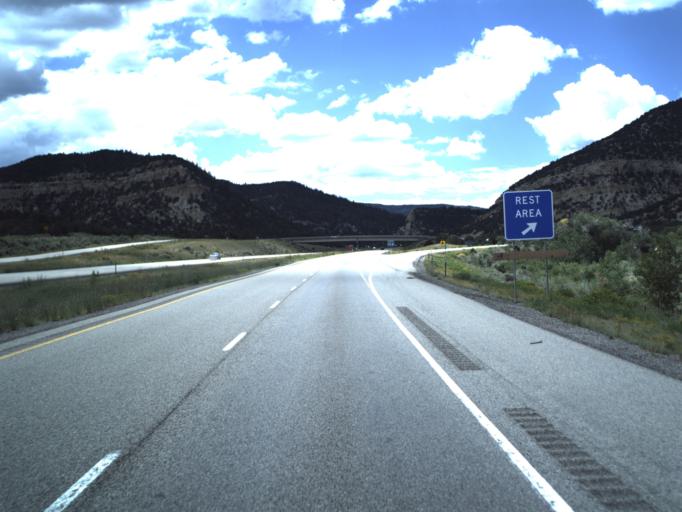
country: US
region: Utah
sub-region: Wayne County
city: Loa
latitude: 38.7573
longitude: -111.4191
